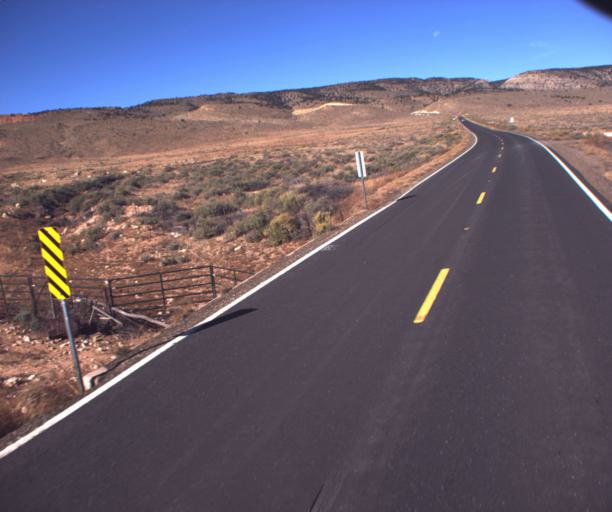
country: US
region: Arizona
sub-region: Coconino County
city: Fredonia
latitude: 36.7311
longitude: -112.0454
